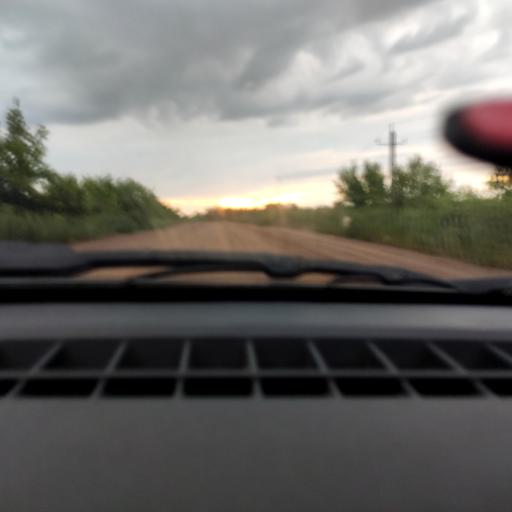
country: RU
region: Bashkortostan
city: Blagoveshchensk
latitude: 54.9195
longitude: 55.9769
